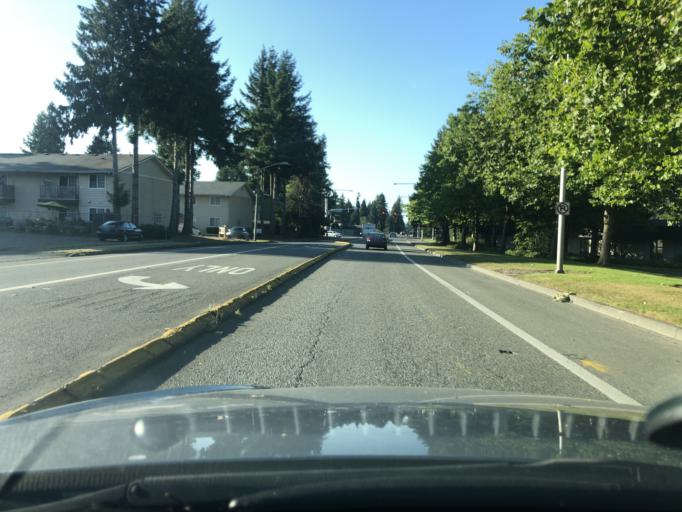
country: US
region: Washington
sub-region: King County
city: Auburn
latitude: 47.2816
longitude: -122.2079
